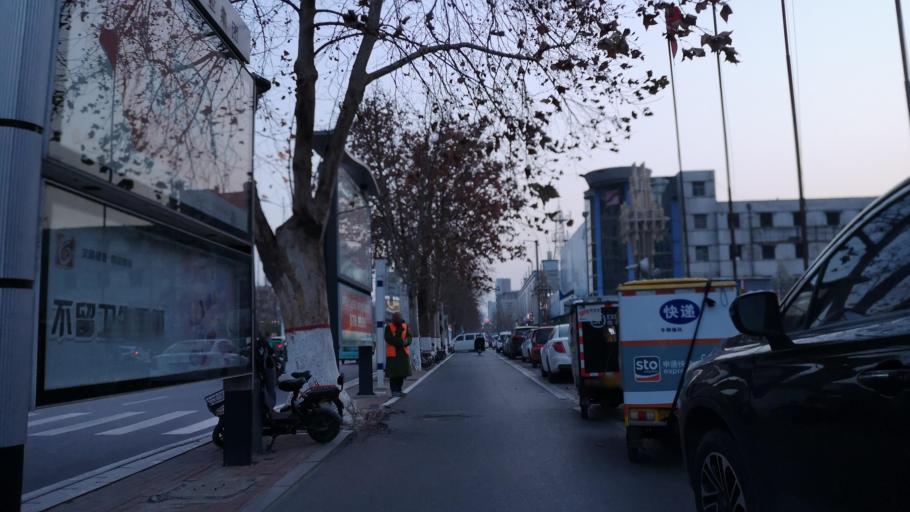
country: CN
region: Henan Sheng
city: Zhongyuanlu
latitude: 35.7752
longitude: 115.0703
